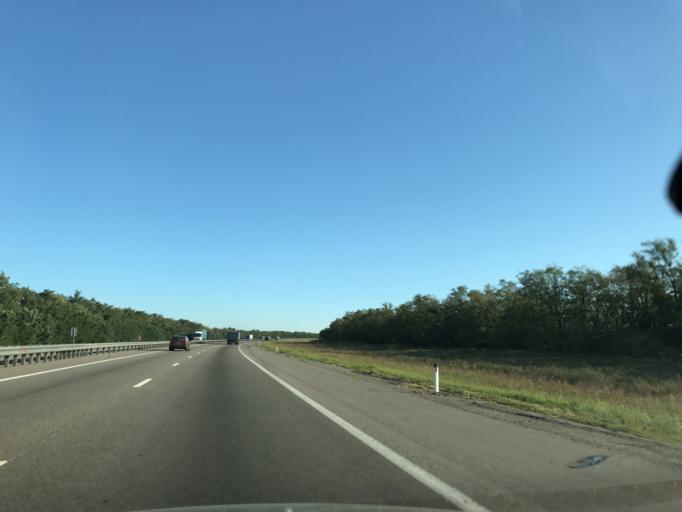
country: RU
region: Rostov
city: Zverevo
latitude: 47.9772
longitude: 40.2178
